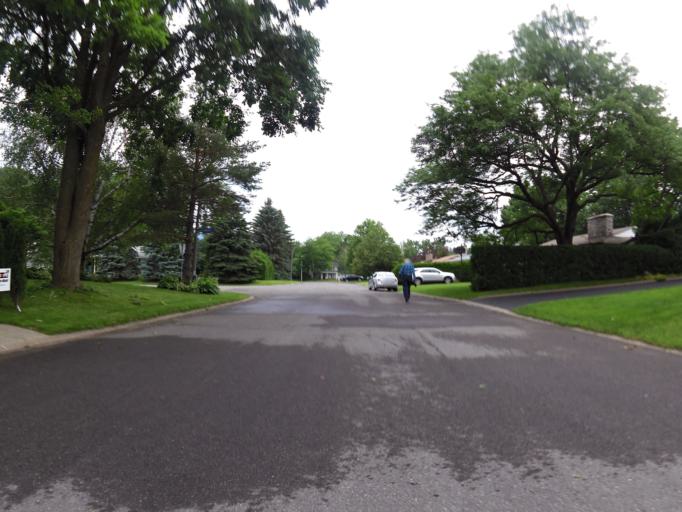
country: CA
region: Ontario
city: Bells Corners
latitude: 45.3392
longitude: -75.7750
